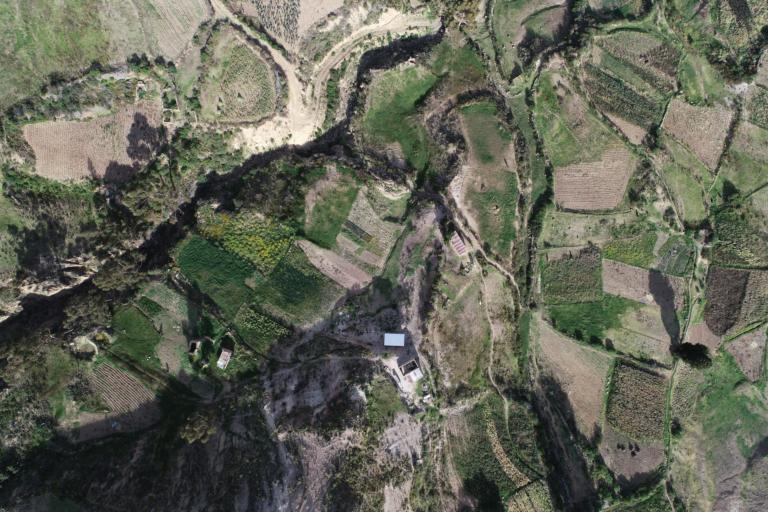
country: BO
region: La Paz
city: La Paz
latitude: -16.5524
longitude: -67.9885
